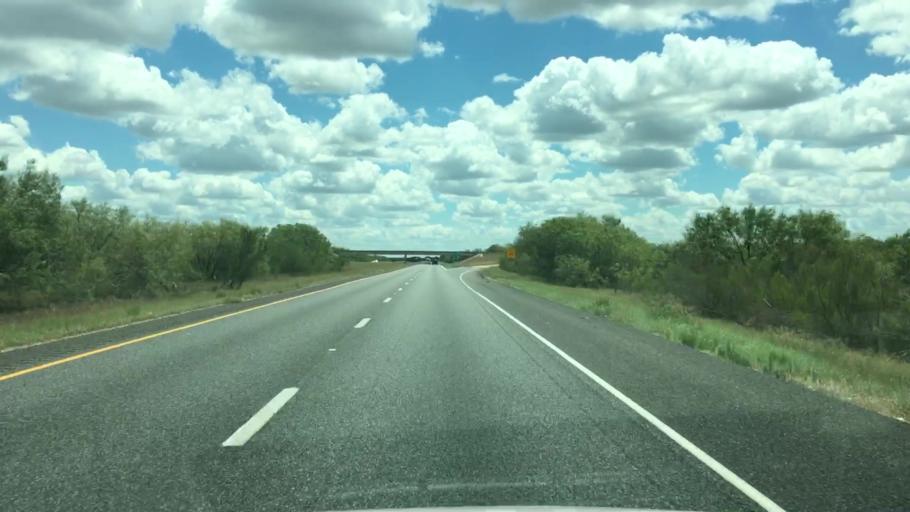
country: US
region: Texas
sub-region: Atascosa County
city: Pleasanton
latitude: 28.9212
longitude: -98.4352
